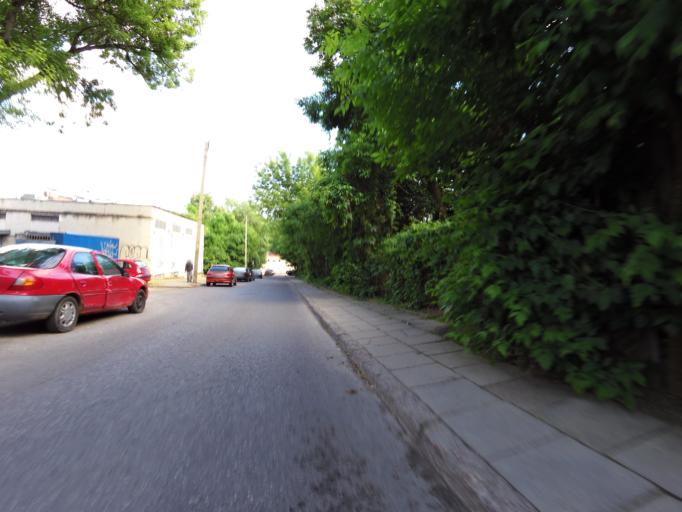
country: LT
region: Vilnius County
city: Naujamiestis
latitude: 54.6709
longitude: 25.2768
